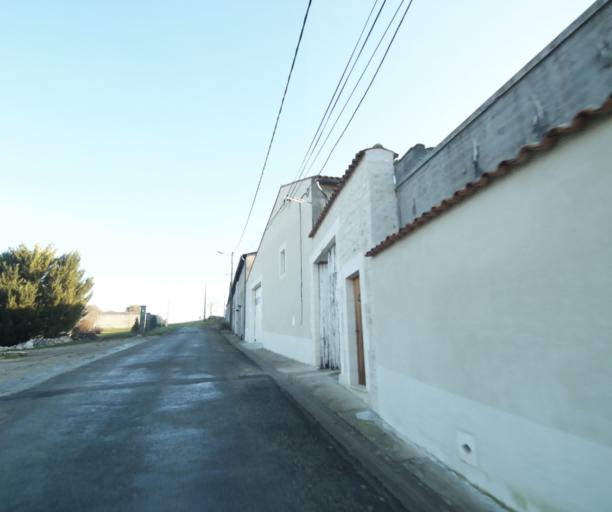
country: FR
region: Poitou-Charentes
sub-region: Departement de la Charente-Maritime
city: Cherac
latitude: 45.6880
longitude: -0.4250
